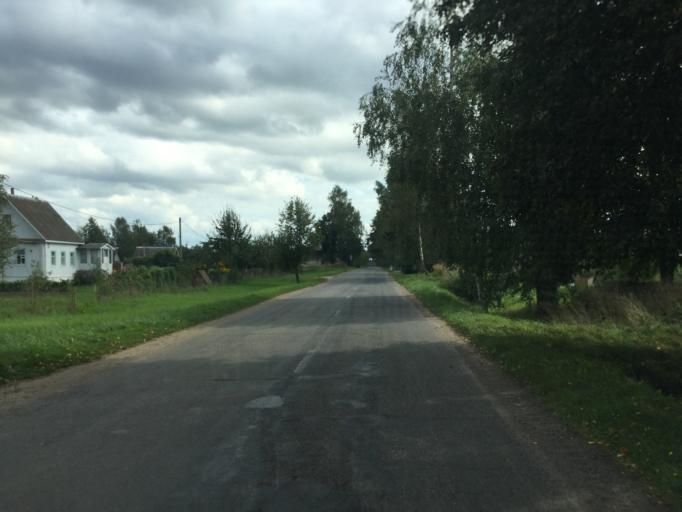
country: BY
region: Vitebsk
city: Vitebsk
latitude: 55.1462
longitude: 30.2825
